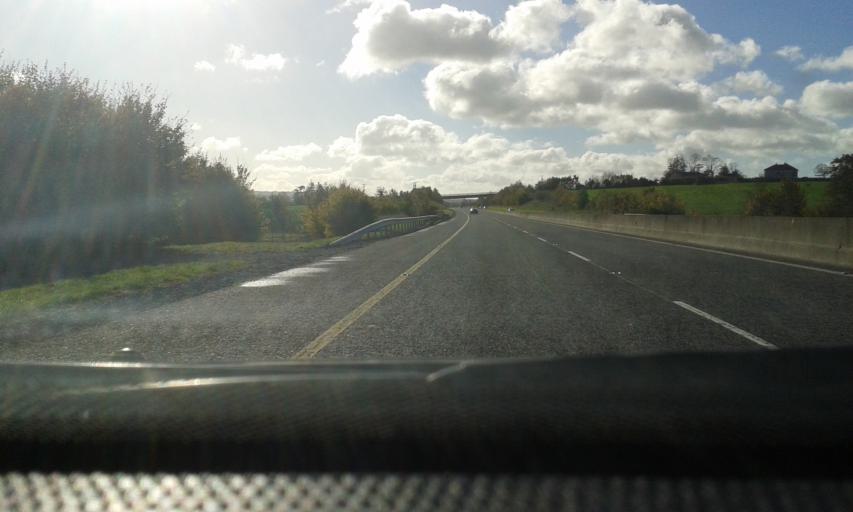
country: IE
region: Munster
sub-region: County Cork
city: Rathcormac
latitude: 52.0922
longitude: -8.2900
